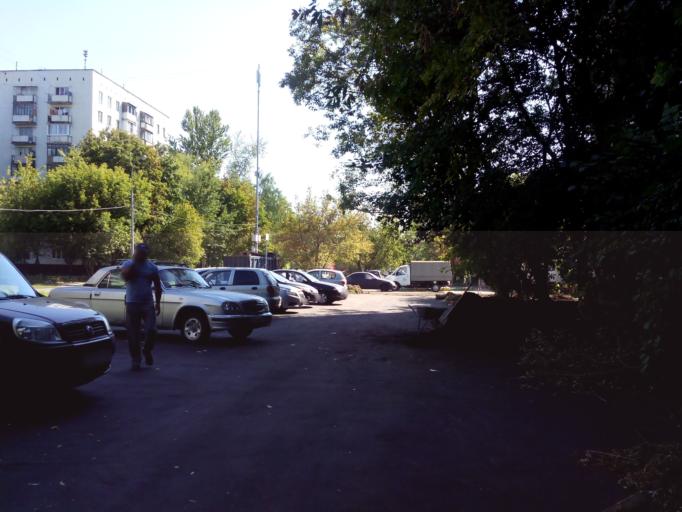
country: RU
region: Moskovskaya
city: Bol'shaya Setun'
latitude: 55.7291
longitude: 37.4175
